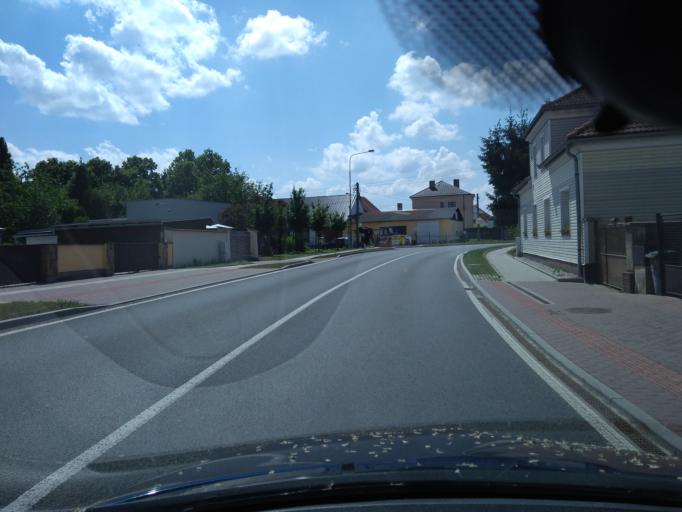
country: CZ
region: Plzensky
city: Prestice
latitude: 49.5484
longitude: 13.3161
